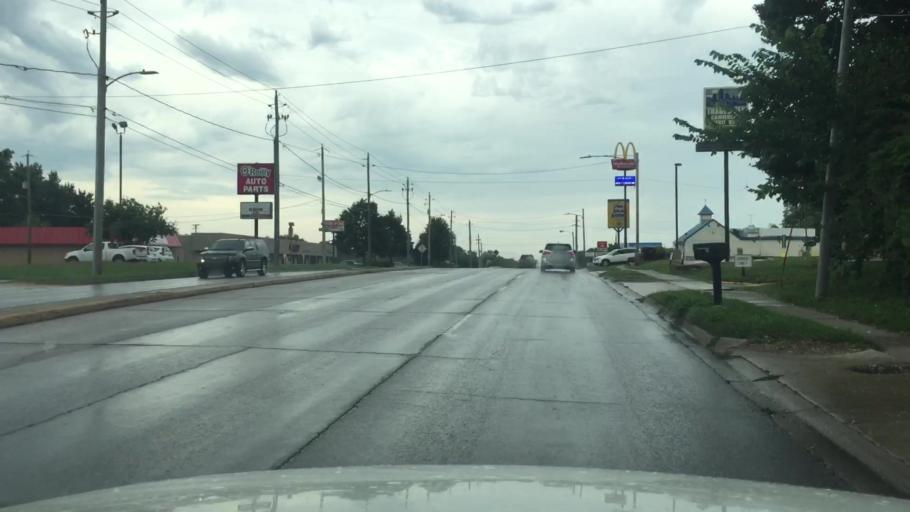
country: US
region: Iowa
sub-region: Polk County
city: Des Moines
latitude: 41.5584
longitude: -93.5970
